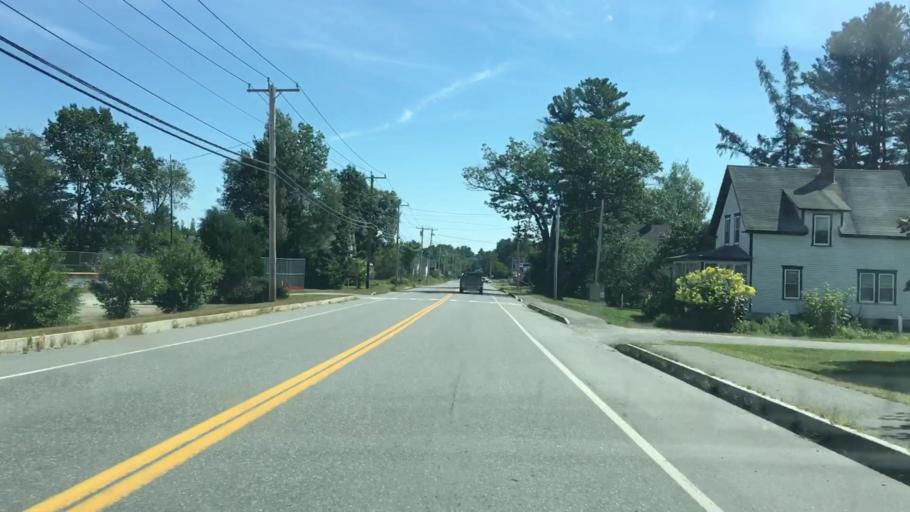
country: US
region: Maine
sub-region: Piscataquis County
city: Milo
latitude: 45.2471
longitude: -68.9781
